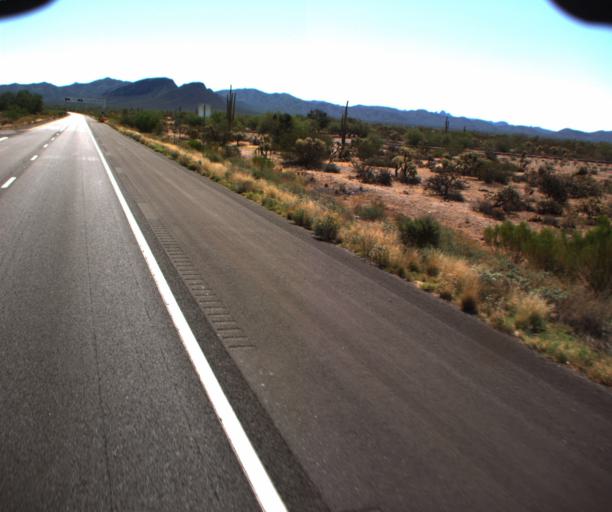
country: US
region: Arizona
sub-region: Pinal County
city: Gold Camp
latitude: 33.2576
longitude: -111.3043
